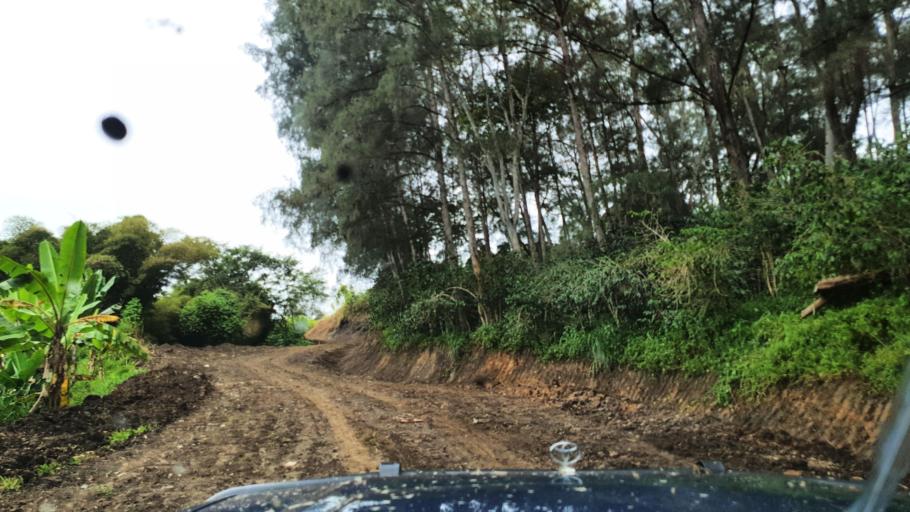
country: PG
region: Jiwaka
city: Minj
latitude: -5.9282
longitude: 144.7414
